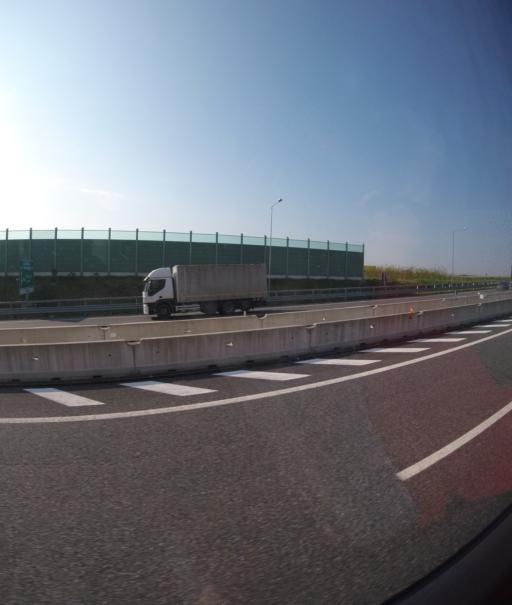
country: IT
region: Lombardy
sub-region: Provincia di Varese
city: Fagnano Olona-Bergoro
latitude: 45.6501
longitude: 8.8451
